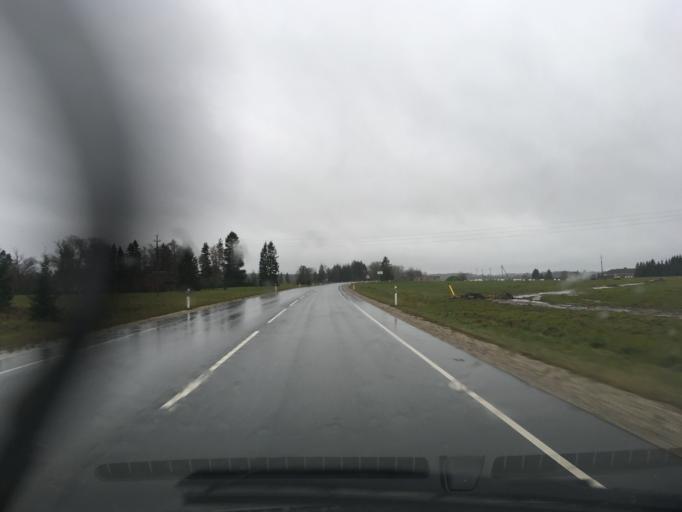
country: EE
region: Harju
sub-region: Nissi vald
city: Turba
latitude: 58.8772
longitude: 24.0870
